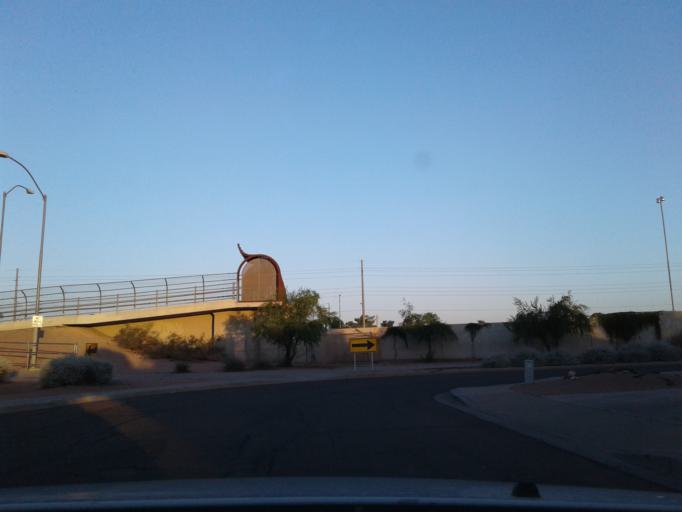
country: US
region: Arizona
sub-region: Maricopa County
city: Paradise Valley
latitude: 33.6335
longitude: -112.0034
